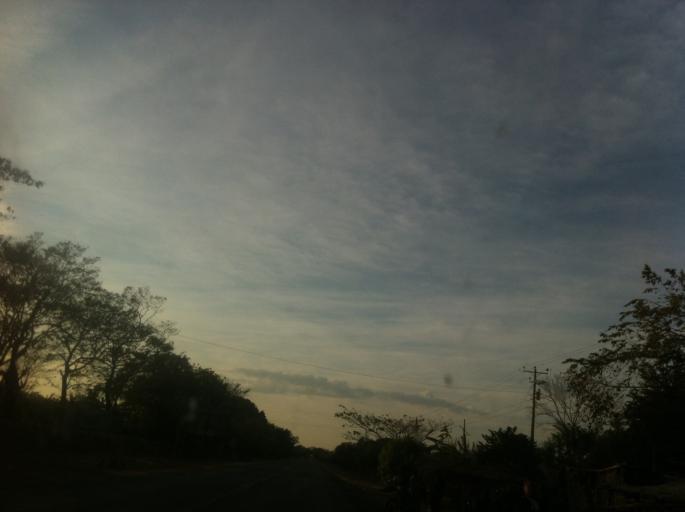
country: NI
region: Rivas
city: Potosi
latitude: 11.4919
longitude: -85.8738
